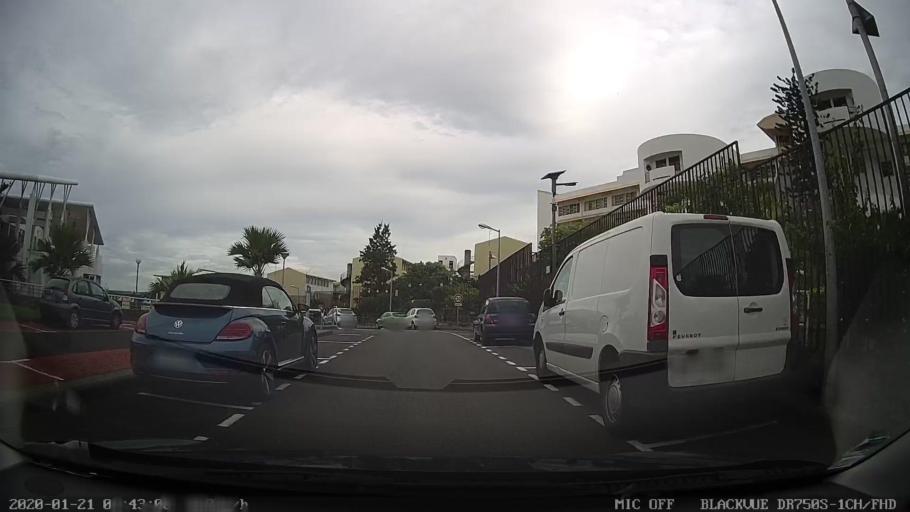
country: RE
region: Reunion
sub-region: Reunion
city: Saint-Denis
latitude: -20.9029
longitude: 55.4828
